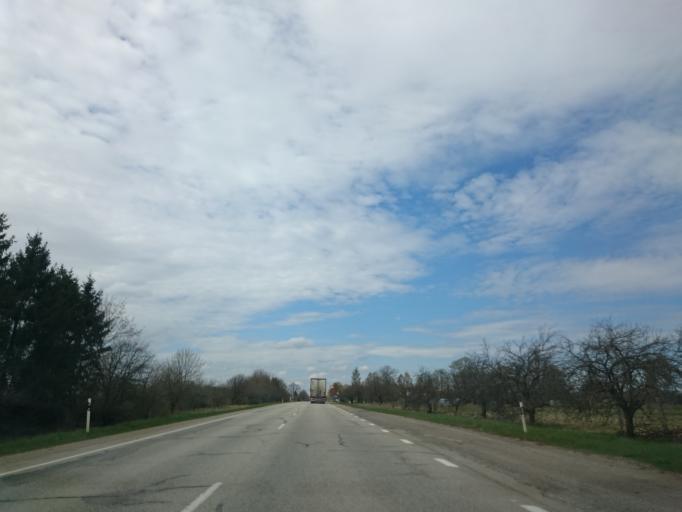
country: LV
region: Tukuma Rajons
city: Tukums
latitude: 56.9287
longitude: 23.2203
